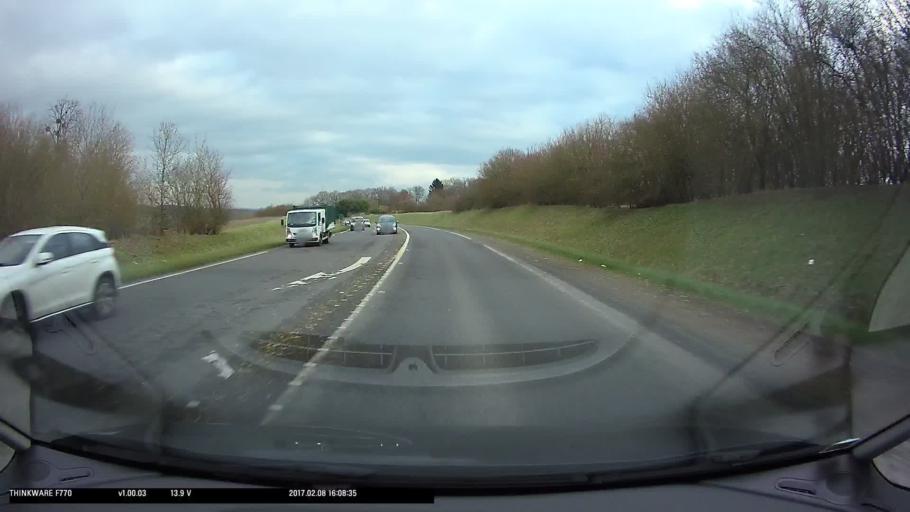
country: FR
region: Ile-de-France
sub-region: Departement du Val-d'Oise
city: Marines
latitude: 49.1235
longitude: 2.0034
